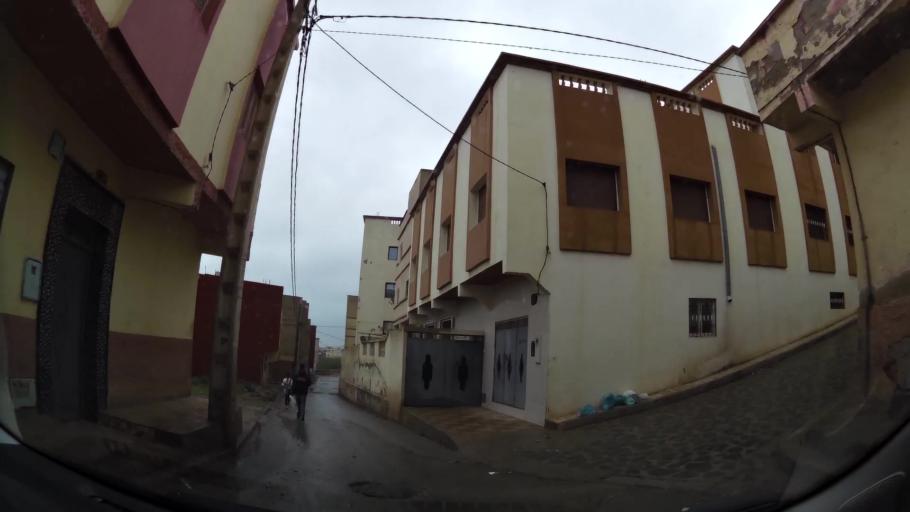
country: MA
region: Oriental
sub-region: Nador
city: Nador
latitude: 35.1788
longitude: -2.9380
